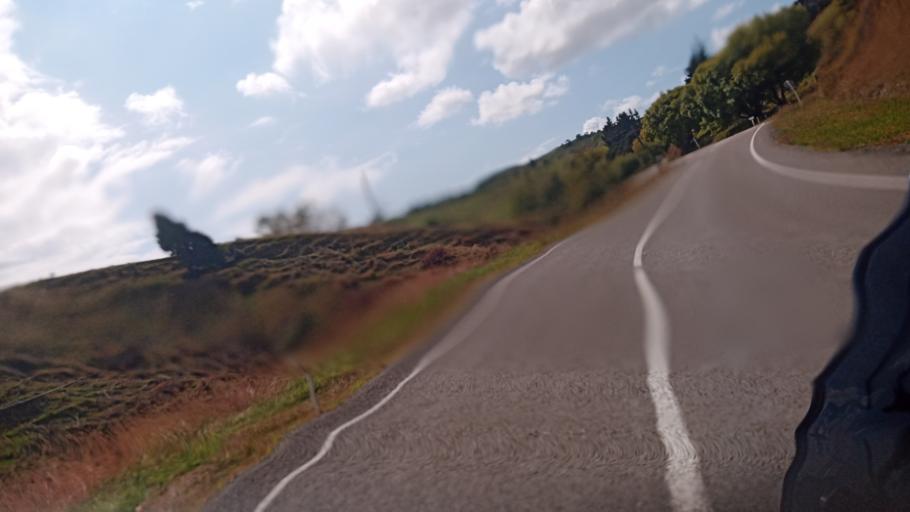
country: NZ
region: Gisborne
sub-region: Gisborne District
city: Gisborne
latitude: -38.1662
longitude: 178.2634
